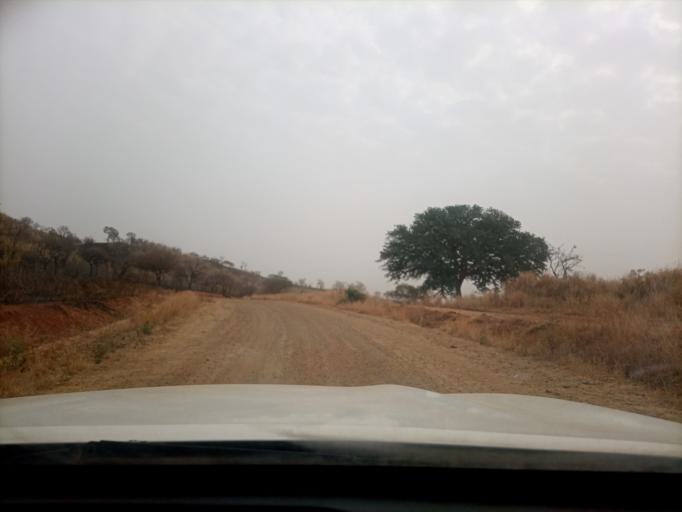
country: ET
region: Oromiya
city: Mendi
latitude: 10.1978
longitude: 35.0658
